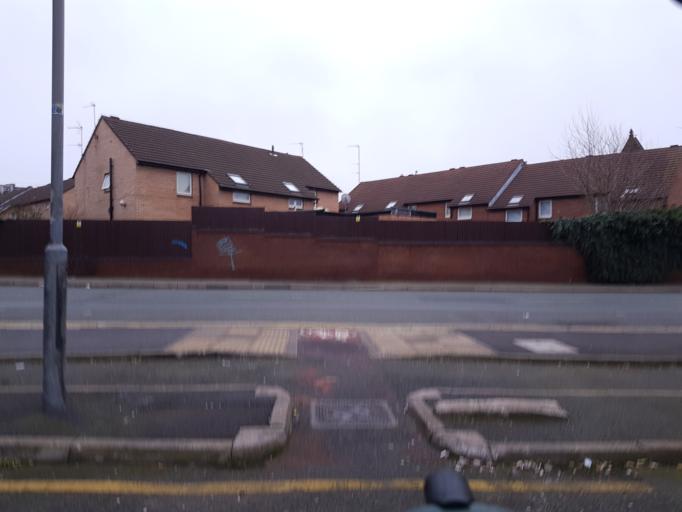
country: GB
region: England
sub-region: Liverpool
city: Liverpool
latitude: 53.4381
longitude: -2.9737
